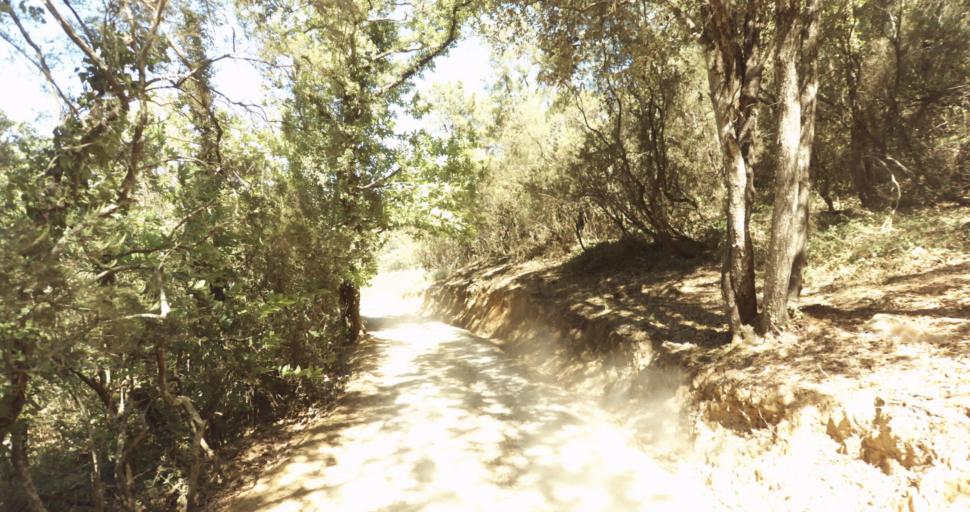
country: FR
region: Provence-Alpes-Cote d'Azur
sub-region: Departement du Var
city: Gassin
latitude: 43.2302
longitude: 6.5650
